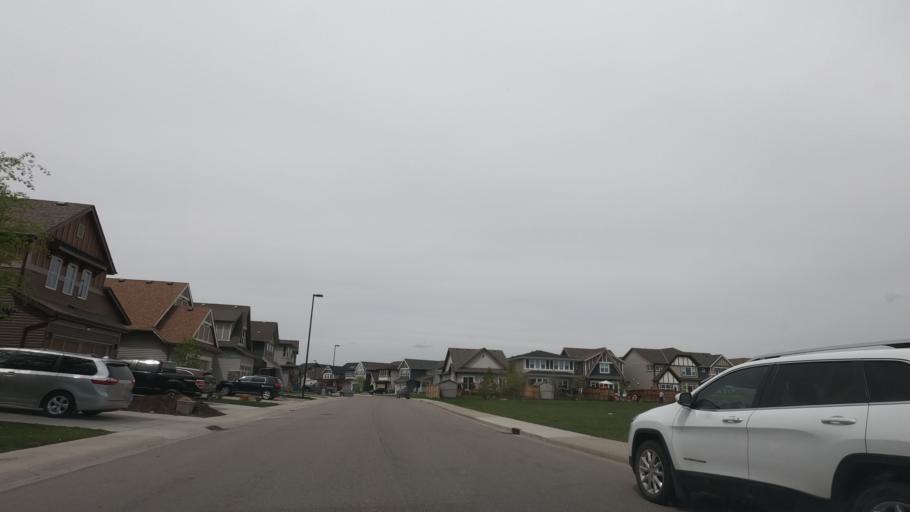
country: CA
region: Alberta
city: Airdrie
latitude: 51.3037
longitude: -114.0401
